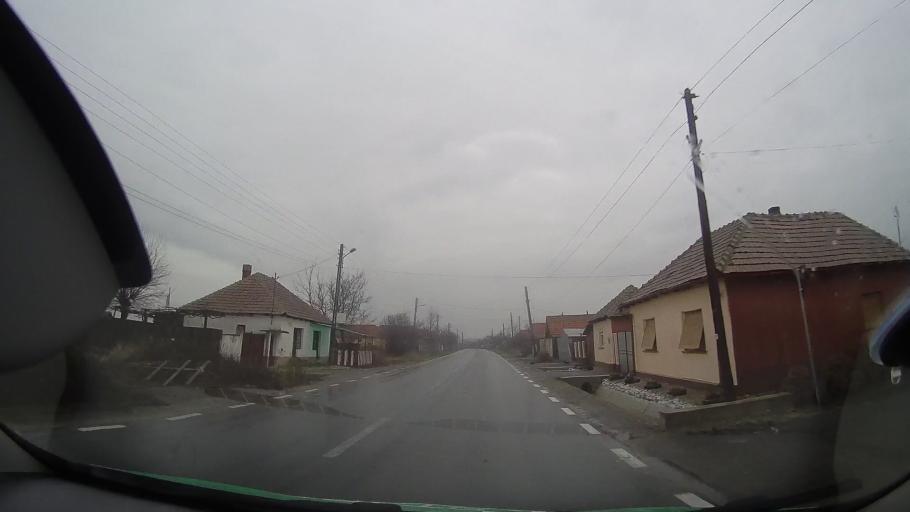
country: RO
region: Bihor
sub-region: Comuna Tinca
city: Tinca
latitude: 46.7353
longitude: 21.9418
